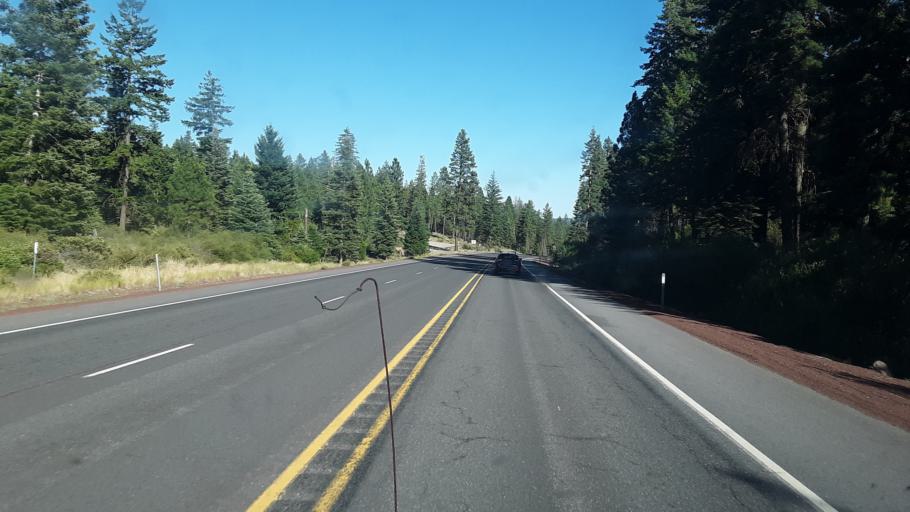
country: US
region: Oregon
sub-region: Klamath County
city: Klamath Falls
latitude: 42.3269
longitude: -121.9524
